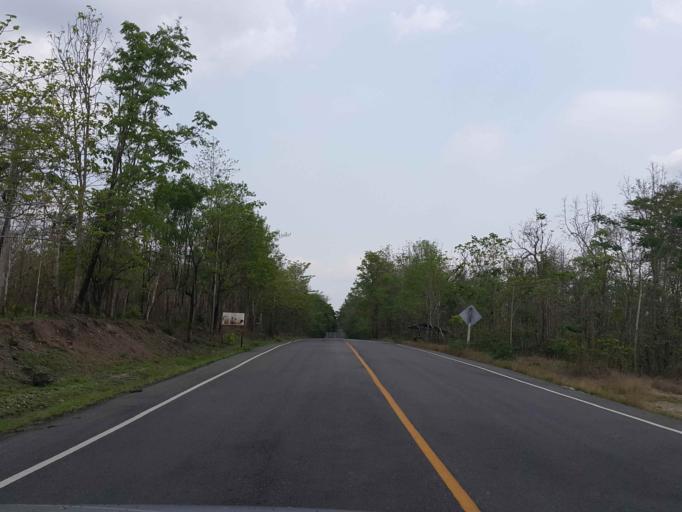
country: TH
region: Sukhothai
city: Thung Saliam
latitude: 17.4151
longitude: 99.3873
